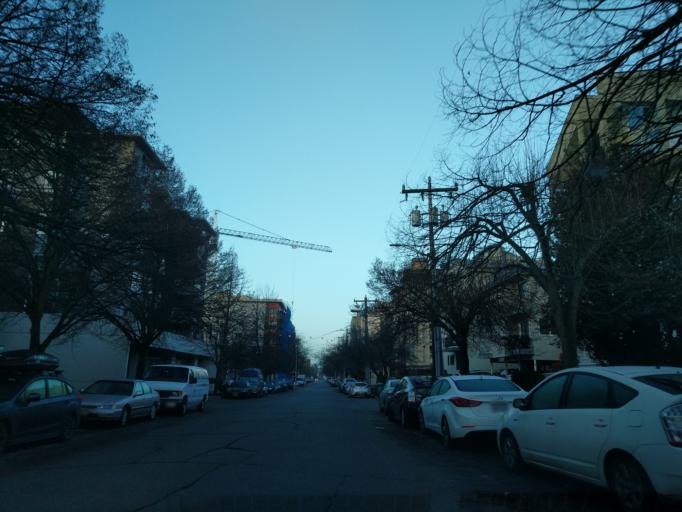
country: US
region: Washington
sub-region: King County
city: Seattle
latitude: 47.6702
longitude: -122.3805
